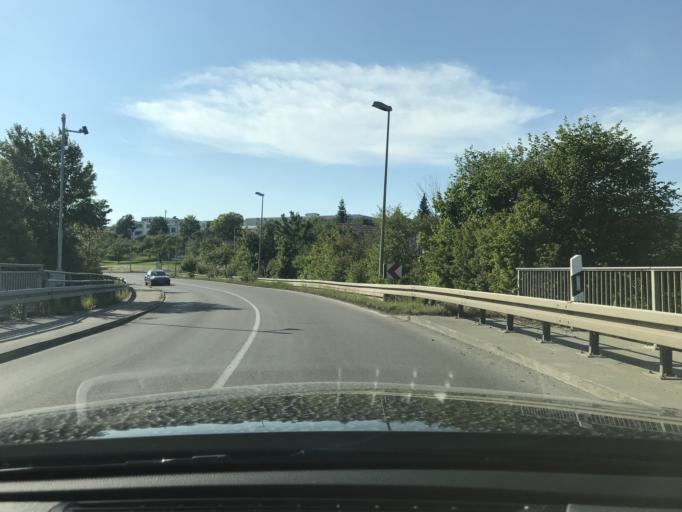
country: DE
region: Baden-Wuerttemberg
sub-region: Regierungsbezirk Stuttgart
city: Schwaikheim
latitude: 48.8610
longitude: 9.3286
